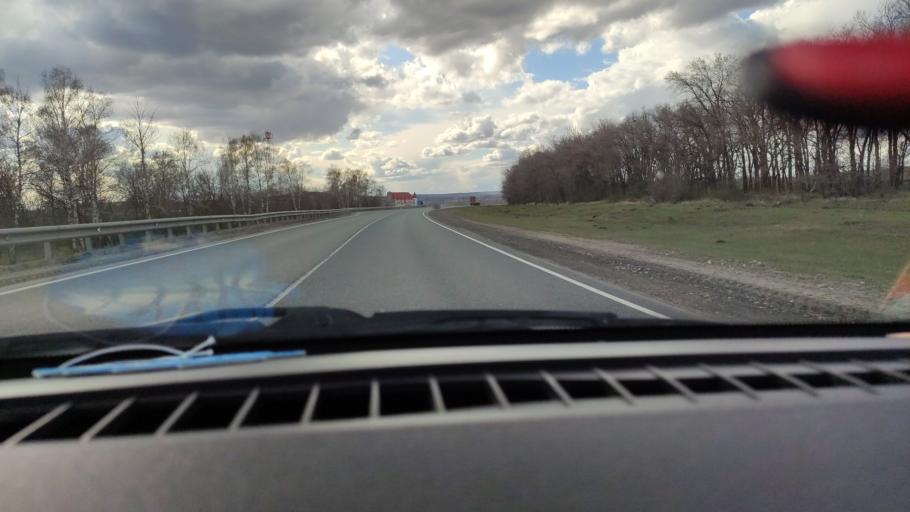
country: RU
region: Saratov
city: Tersa
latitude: 52.0842
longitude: 47.5545
